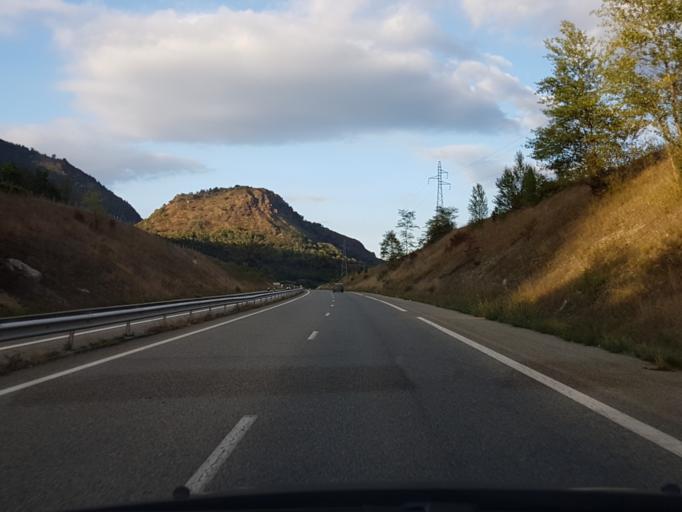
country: FR
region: Midi-Pyrenees
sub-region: Departement de l'Ariege
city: Tarascon-sur-Ariege
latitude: 42.8619
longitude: 1.6008
